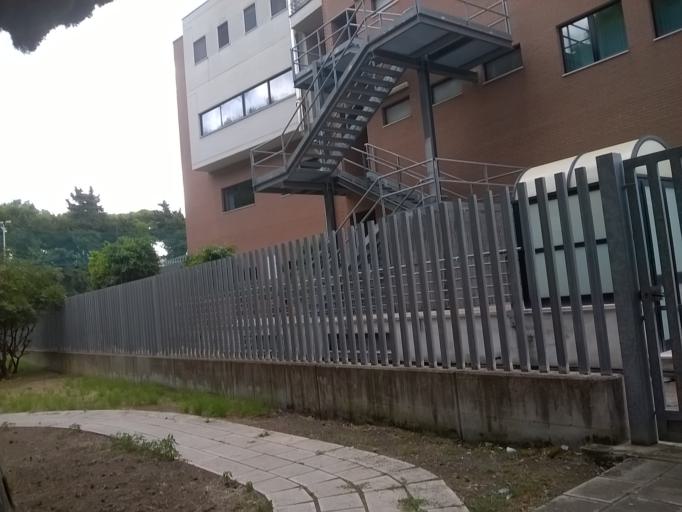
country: IT
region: Apulia
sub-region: Provincia di Taranto
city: Taranto
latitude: 40.4597
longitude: 17.2713
